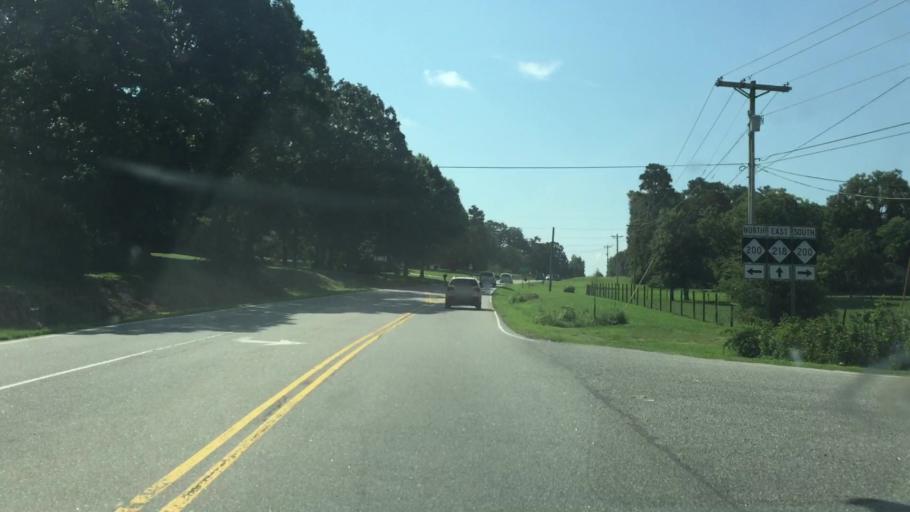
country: US
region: North Carolina
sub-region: Union County
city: Unionville
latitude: 35.1285
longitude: -80.4320
